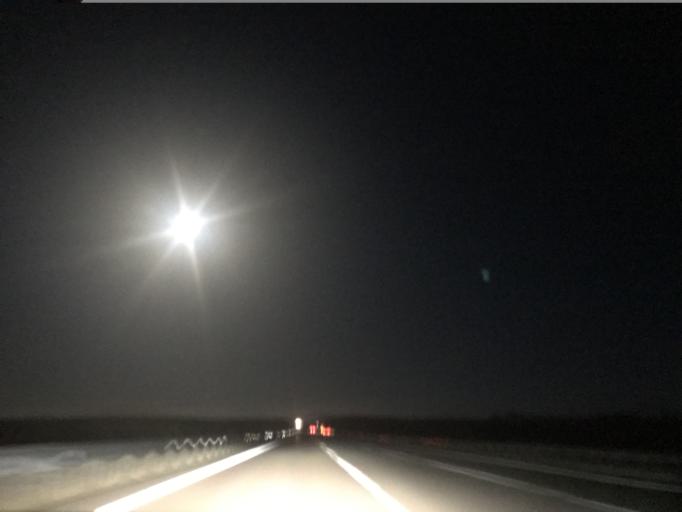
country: TR
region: Nigde
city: Ulukisla
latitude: 37.6385
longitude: 34.3939
